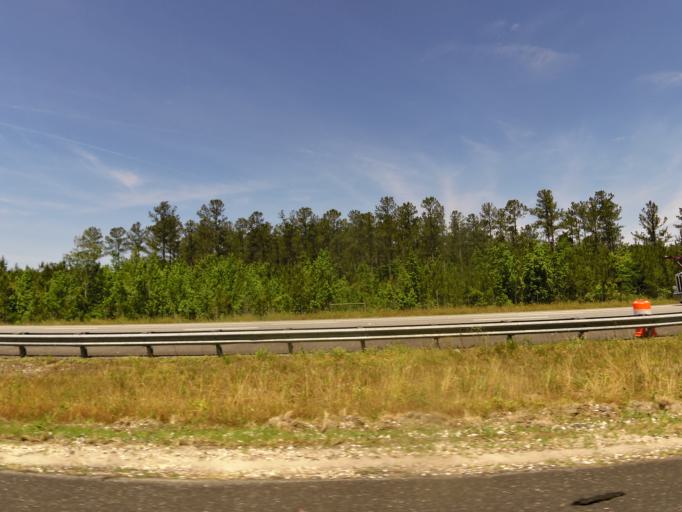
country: US
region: Georgia
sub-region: Camden County
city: Woodbine
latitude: 31.0538
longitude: -81.6421
